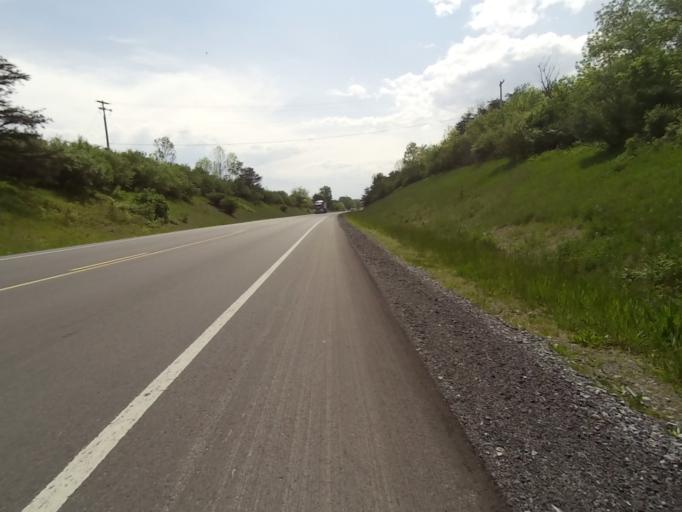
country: US
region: Pennsylvania
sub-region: Centre County
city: Zion
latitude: 41.0393
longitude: -77.6465
